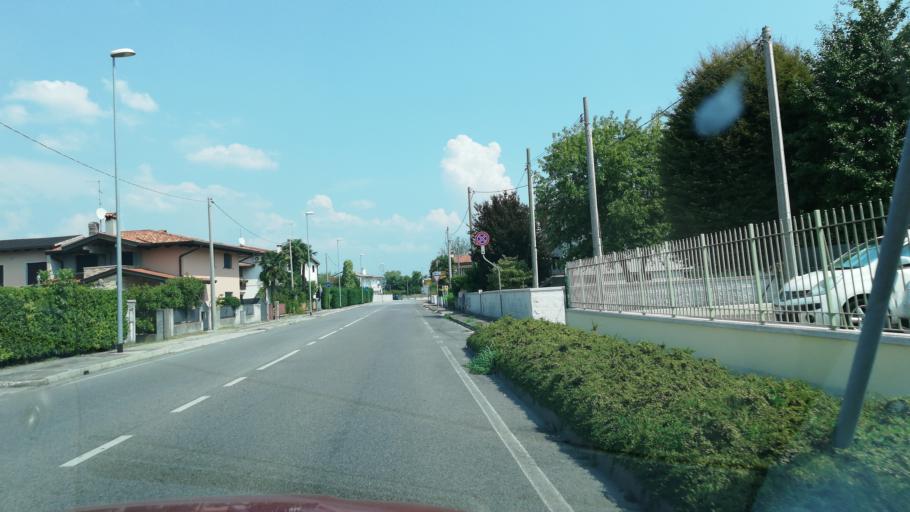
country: IT
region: Friuli Venezia Giulia
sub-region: Provincia di Udine
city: Latisana
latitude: 45.7914
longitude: 13.0177
